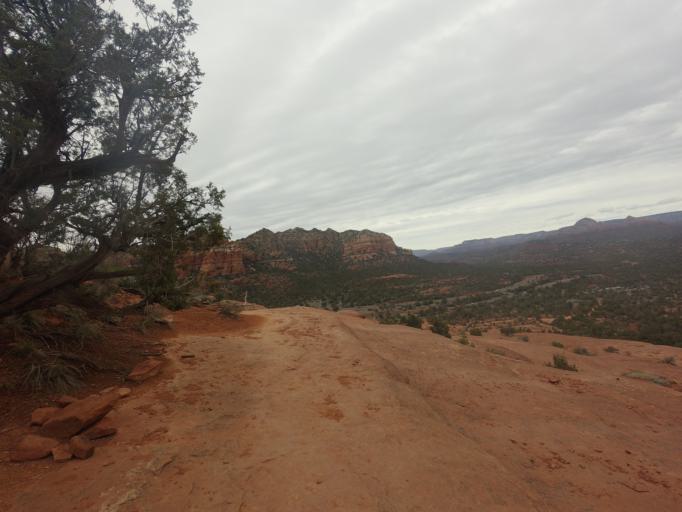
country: US
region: Arizona
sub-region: Yavapai County
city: Village of Oak Creek (Big Park)
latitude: 34.8013
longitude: -111.7646
